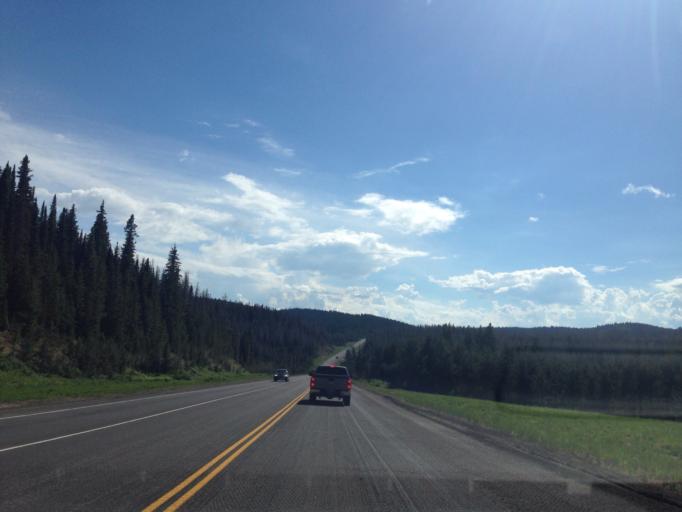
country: US
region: Colorado
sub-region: Routt County
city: Steamboat Springs
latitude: 40.3837
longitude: -106.7093
